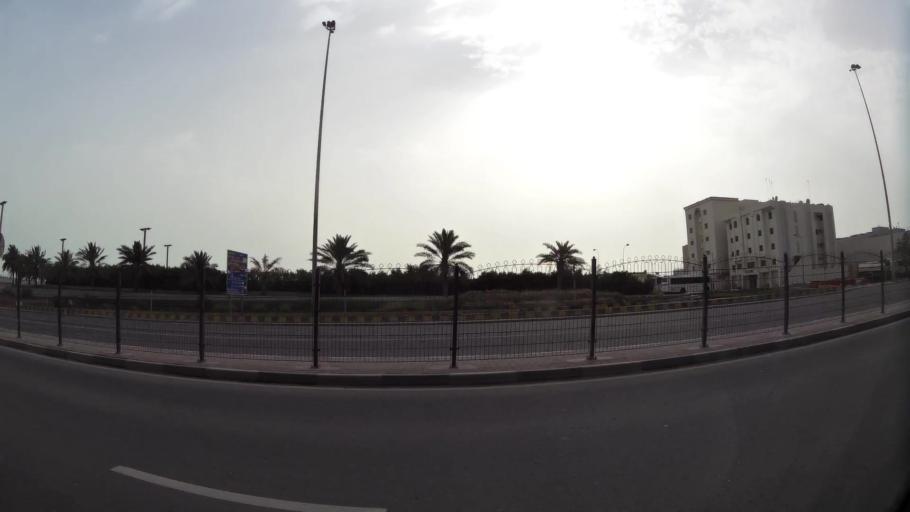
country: QA
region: Baladiyat ad Dawhah
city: Doha
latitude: 25.2821
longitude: 51.5517
